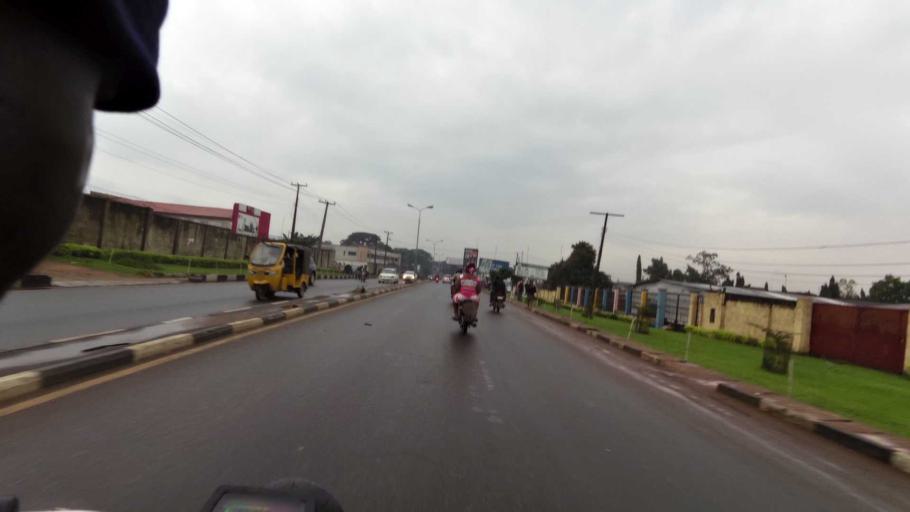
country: NG
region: Oyo
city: Ibadan
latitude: 7.4014
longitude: 3.9244
